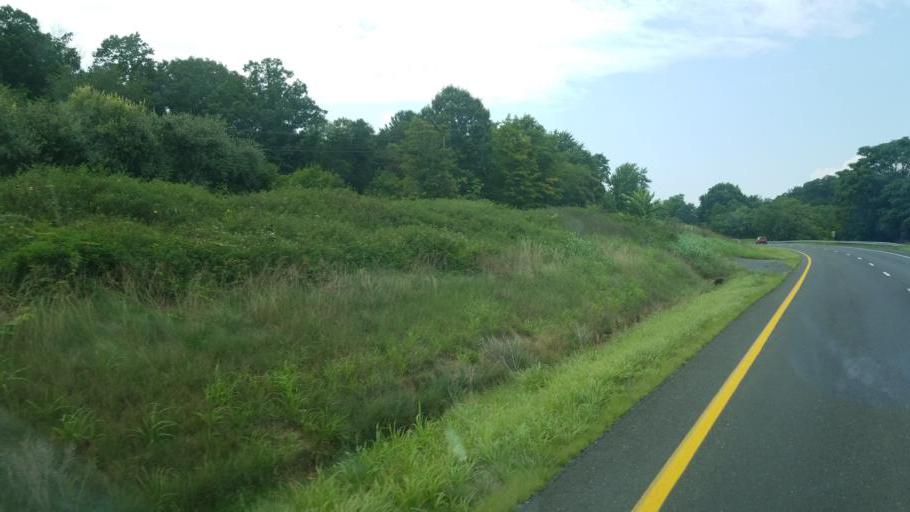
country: US
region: Virginia
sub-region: City of Winchester
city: Winchester
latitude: 39.2593
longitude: -78.2205
